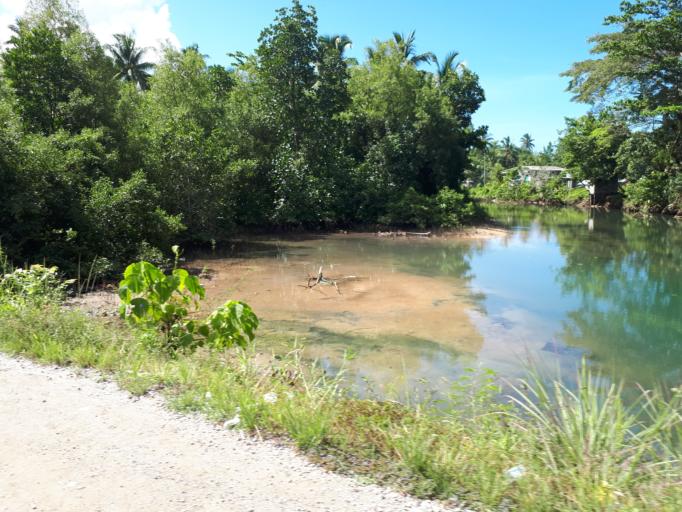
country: SB
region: Malaita
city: Auki
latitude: -8.7719
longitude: 160.7011
